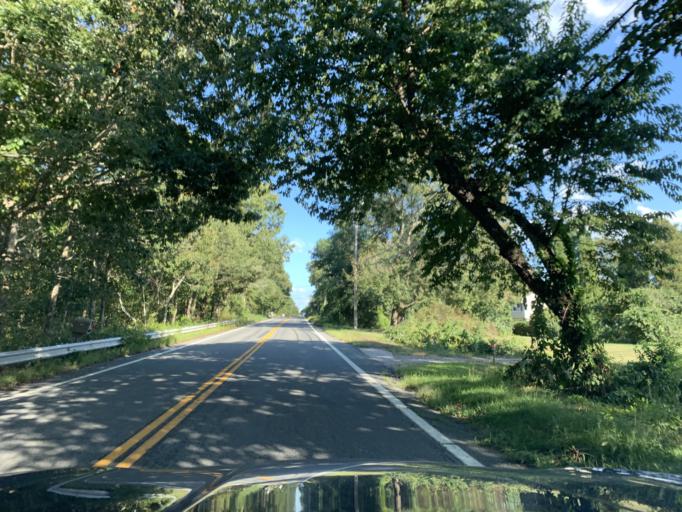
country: US
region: Rhode Island
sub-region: Washington County
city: Exeter
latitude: 41.5432
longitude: -71.5135
